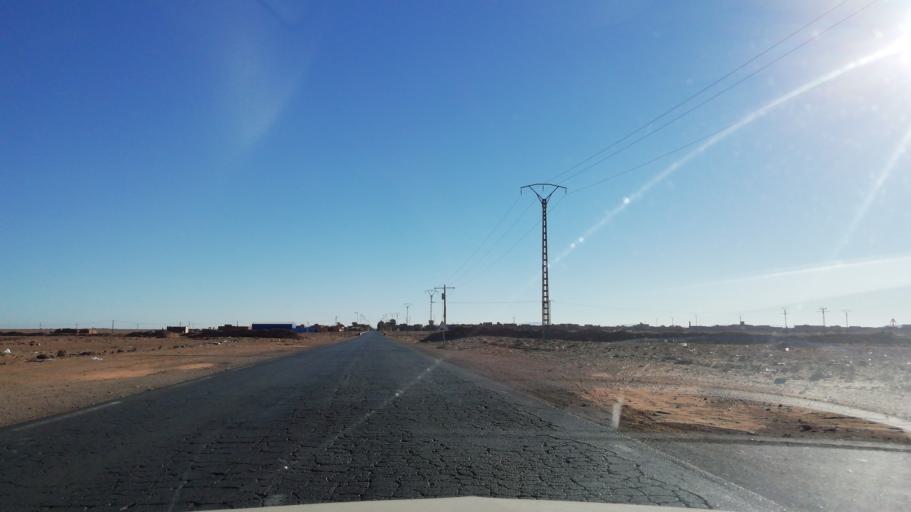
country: DZ
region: El Bayadh
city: El Bayadh
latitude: 33.8534
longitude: 0.6200
